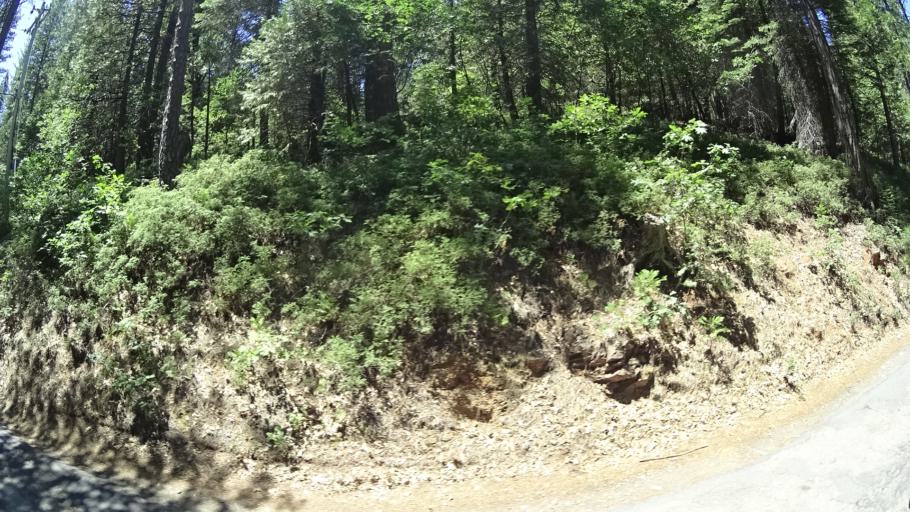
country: US
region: California
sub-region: Calaveras County
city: Arnold
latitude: 38.2220
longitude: -120.3589
